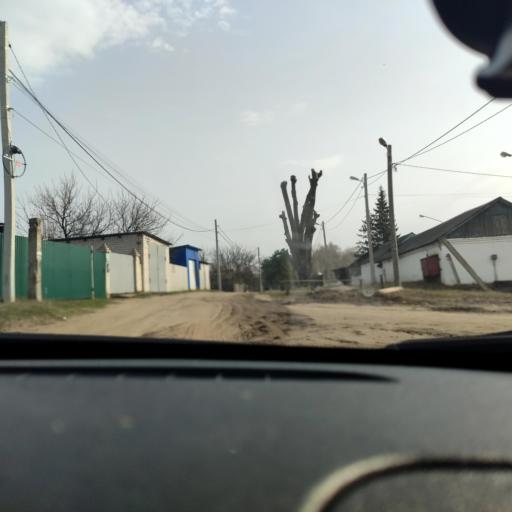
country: RU
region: Voronezj
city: Maslovka
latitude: 51.5645
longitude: 39.2427
